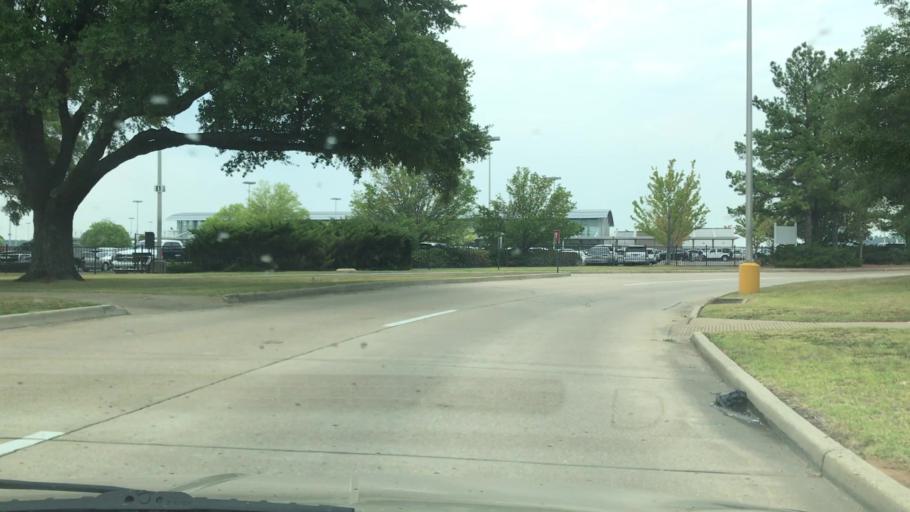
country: US
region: Louisiana
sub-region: Caddo Parish
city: Shreveport
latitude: 32.4562
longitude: -93.8272
